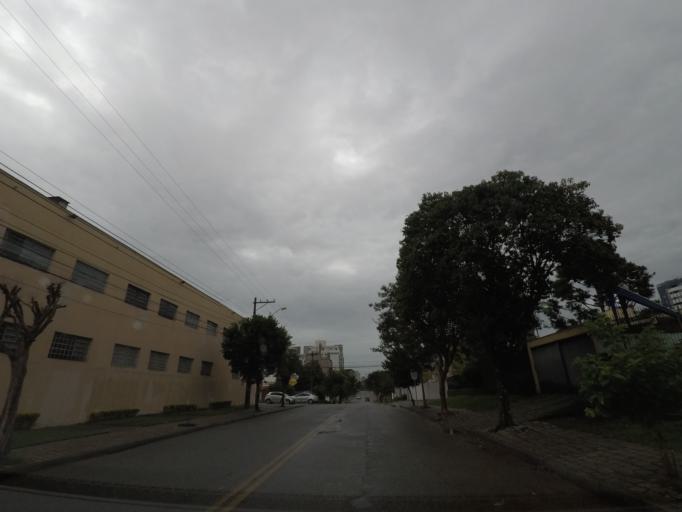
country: BR
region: Parana
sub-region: Curitiba
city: Curitiba
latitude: -25.4611
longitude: -49.2868
